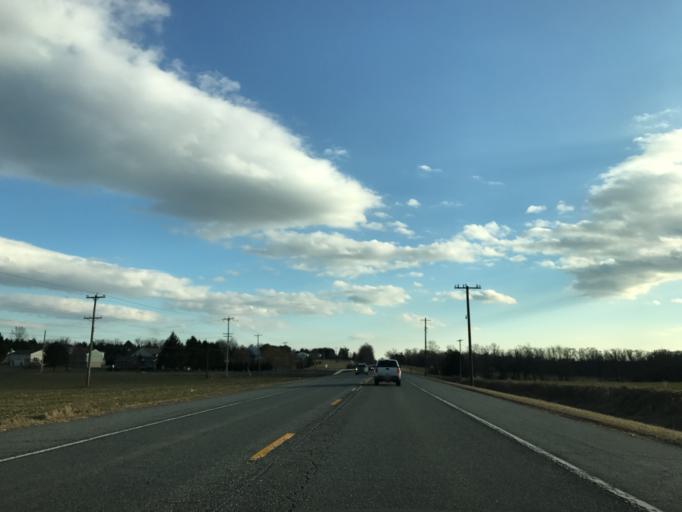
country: US
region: Maryland
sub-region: Cecil County
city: North East
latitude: 39.6639
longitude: -75.9559
